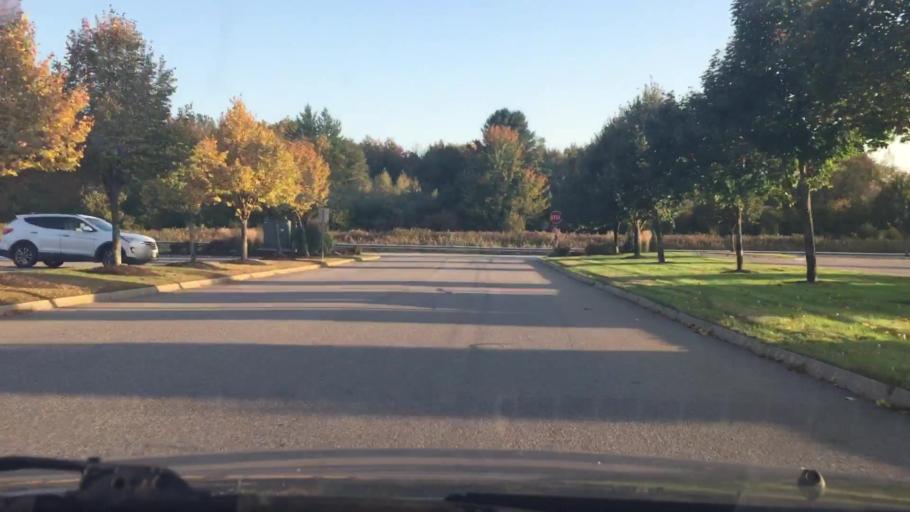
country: US
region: New Hampshire
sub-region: Cheshire County
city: Keene
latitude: 42.9272
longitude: -72.3043
